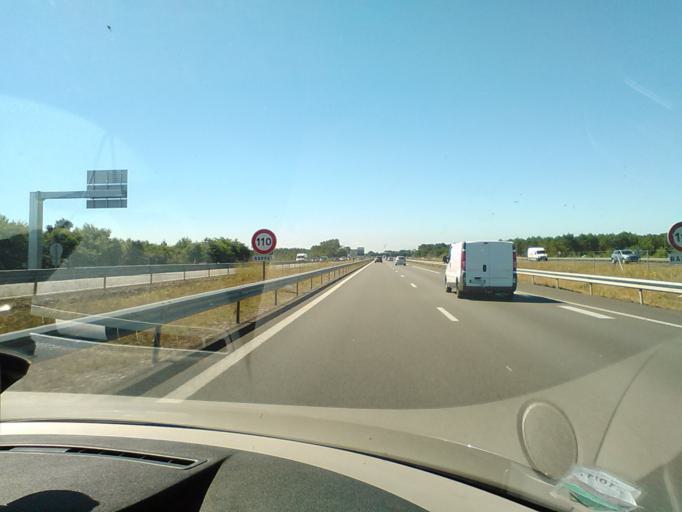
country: FR
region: Aquitaine
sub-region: Departement des Landes
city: Saint-Geours-de-Maremne
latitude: 43.7081
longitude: -1.2284
